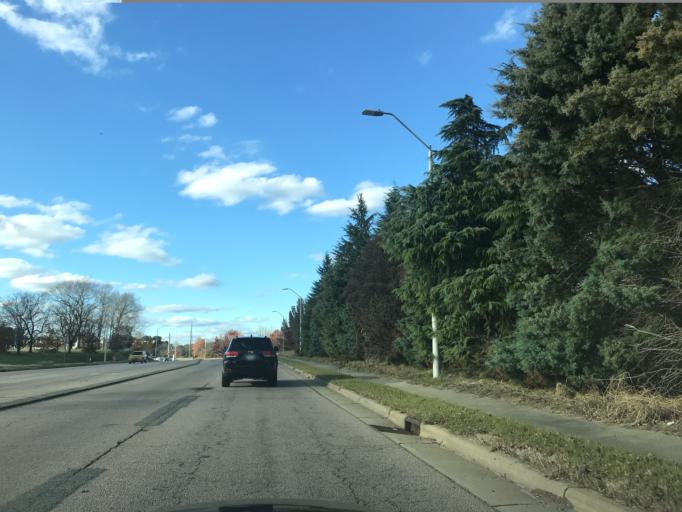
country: US
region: North Carolina
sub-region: Wake County
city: Raleigh
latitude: 35.8650
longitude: -78.5799
